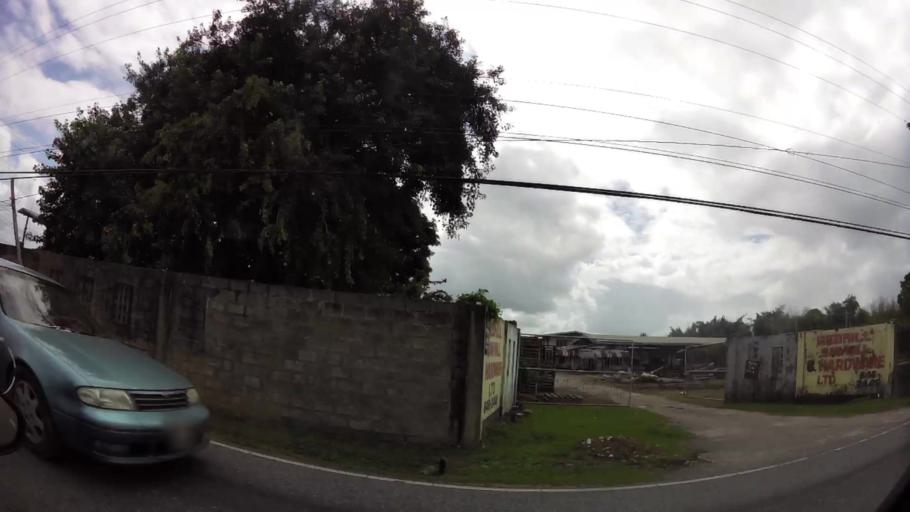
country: TT
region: Tunapuna/Piarco
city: Arouca
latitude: 10.6293
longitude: -61.3162
